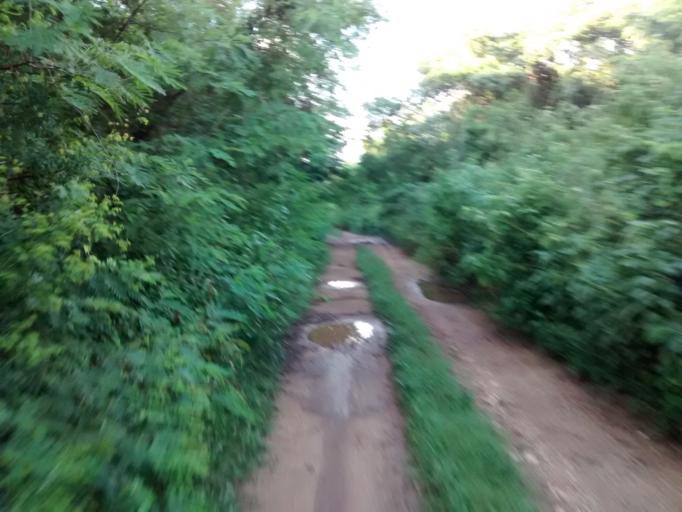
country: MX
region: Yucatan
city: Valladolid
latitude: 20.7177
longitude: -88.2061
